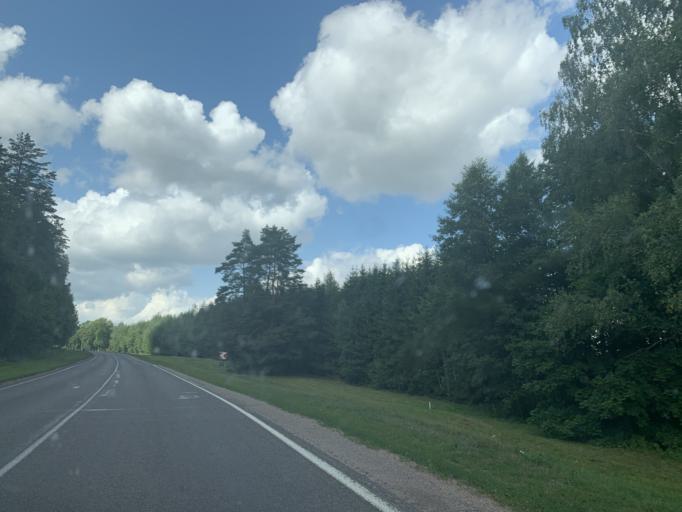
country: BY
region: Minsk
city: Enyerhyetykaw
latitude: 53.5700
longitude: 27.0633
